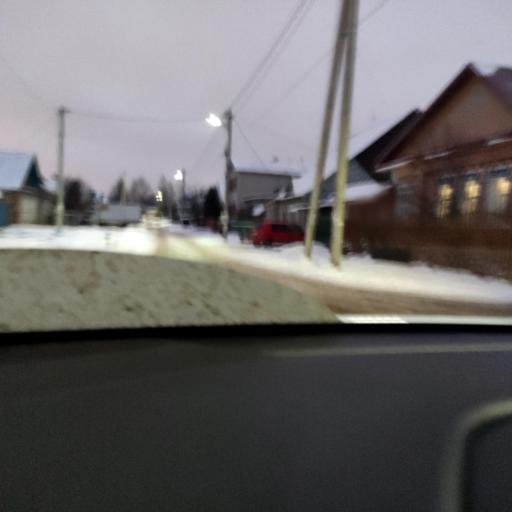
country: RU
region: Tatarstan
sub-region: Gorod Kazan'
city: Kazan
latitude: 55.8796
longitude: 49.0767
